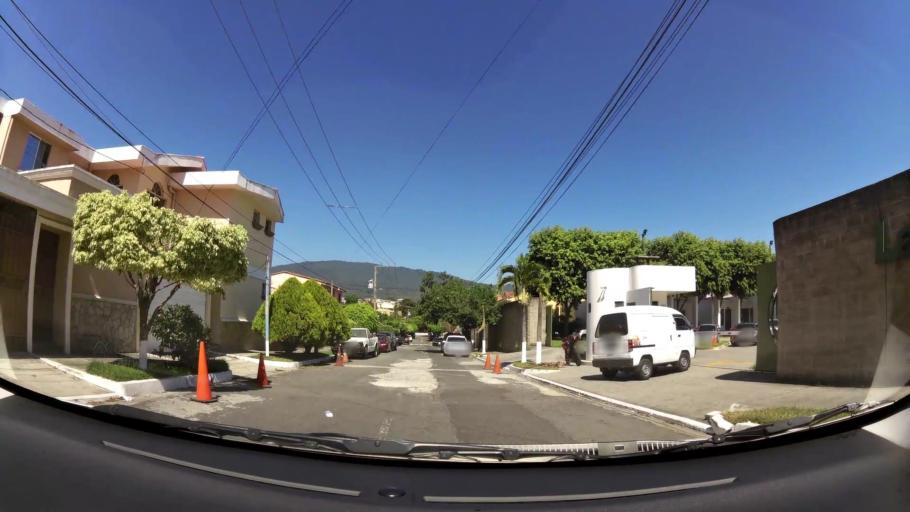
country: SV
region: La Libertad
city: Santa Tecla
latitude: 13.6653
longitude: -89.2794
